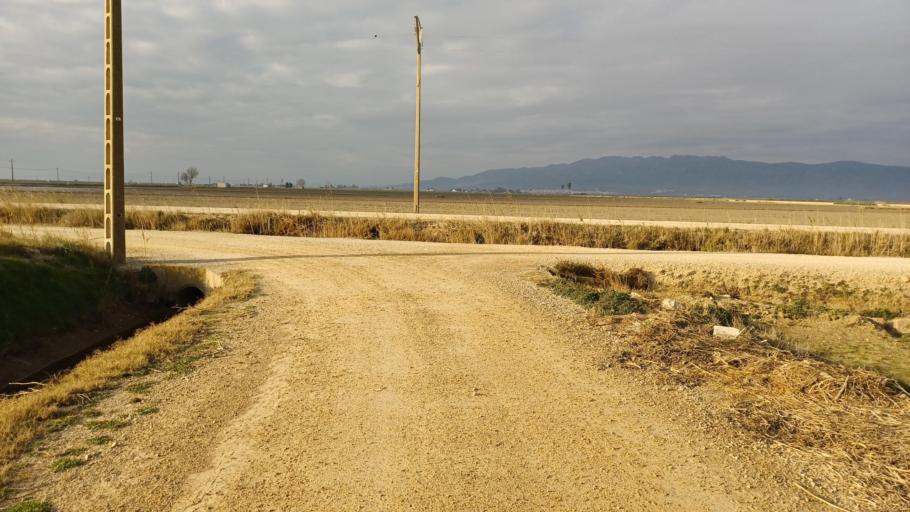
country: ES
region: Catalonia
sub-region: Provincia de Tarragona
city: Deltebre
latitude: 40.6442
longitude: 0.6810
